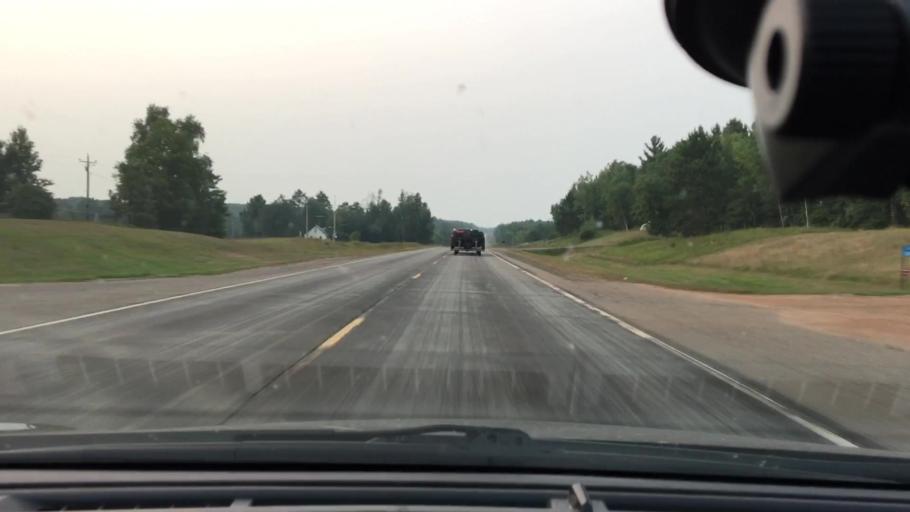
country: US
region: Minnesota
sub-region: Crow Wing County
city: Cross Lake
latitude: 46.6866
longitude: -93.9539
